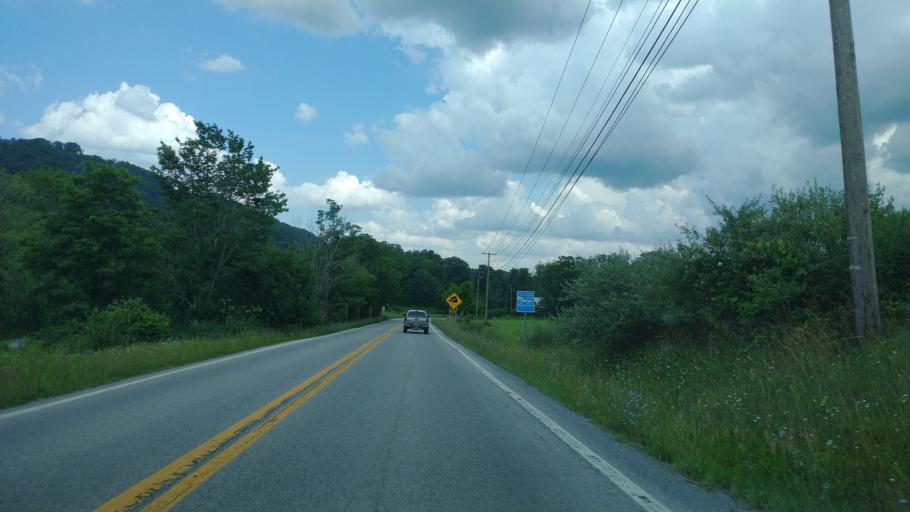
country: US
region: West Virginia
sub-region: Mercer County
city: Athens
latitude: 37.4490
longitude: -81.0047
